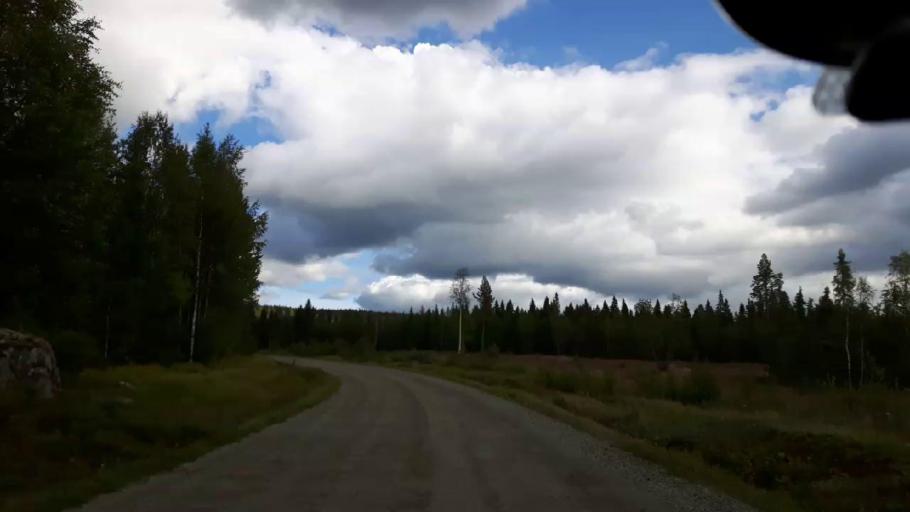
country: SE
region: Jaemtland
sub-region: Stroemsunds Kommun
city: Stroemsund
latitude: 63.3936
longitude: 15.7652
